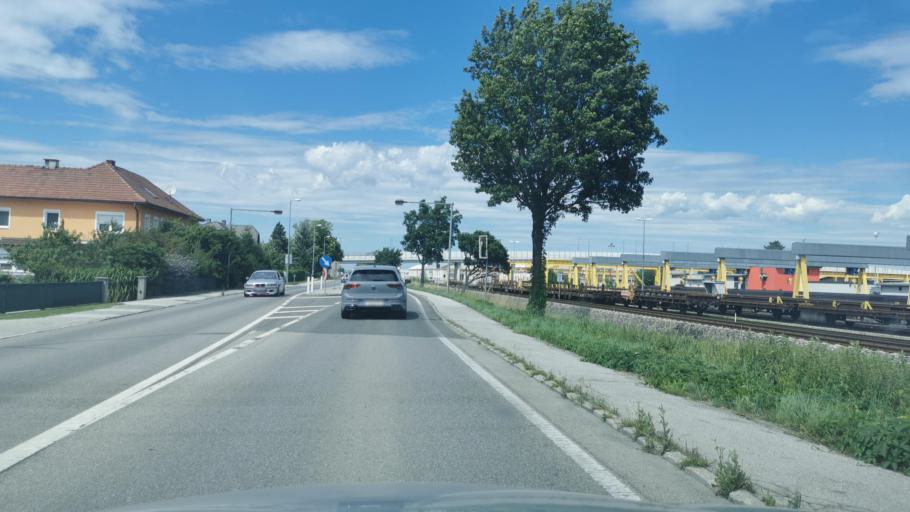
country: AT
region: Lower Austria
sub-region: Politischer Bezirk Sankt Polten
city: Wilhelmsburg
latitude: 48.1502
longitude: 15.6143
